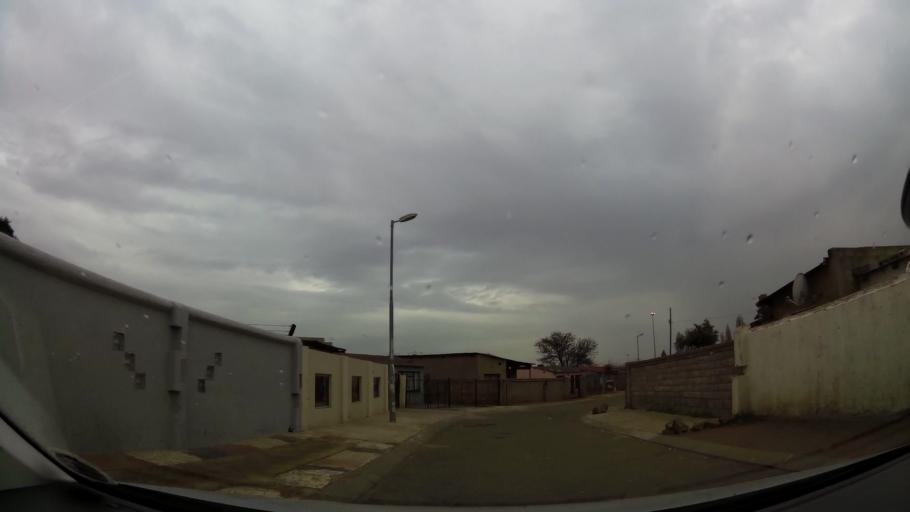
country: ZA
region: Gauteng
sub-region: City of Johannesburg Metropolitan Municipality
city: Soweto
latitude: -26.2546
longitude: 27.8626
